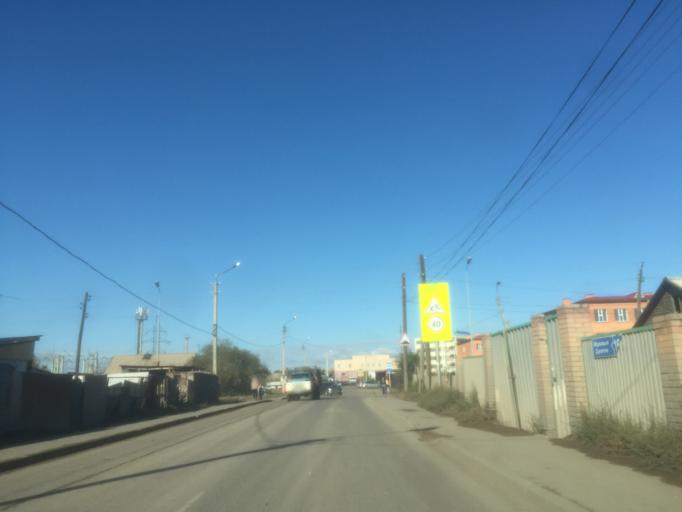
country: KZ
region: Astana Qalasy
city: Astana
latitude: 51.1998
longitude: 71.3663
